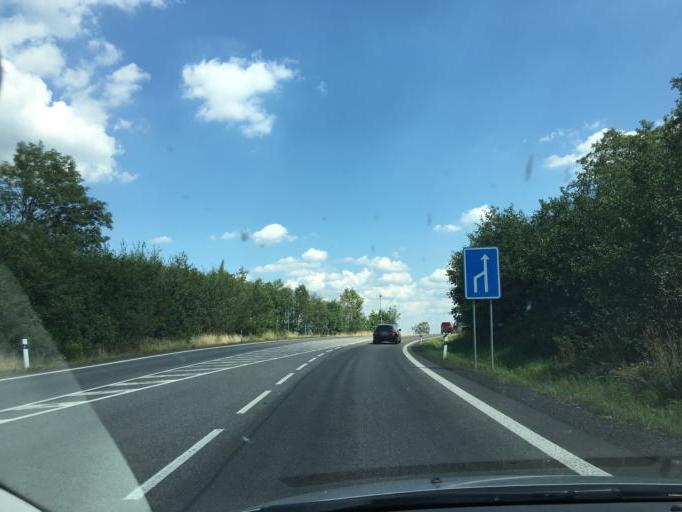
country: CZ
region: Ustecky
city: Benesov nad Ploucnici
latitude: 50.7891
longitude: 14.2855
